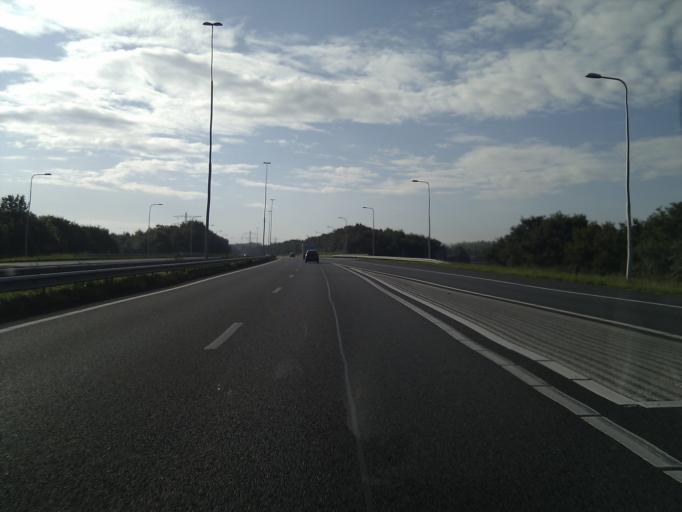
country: NL
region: North Brabant
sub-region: Gemeente Cuijk
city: Cuijk
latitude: 51.7317
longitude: 5.8485
